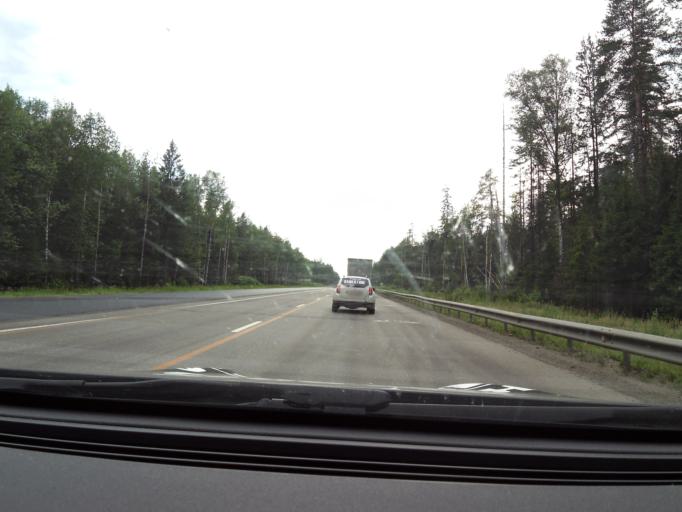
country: RU
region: Vladimir
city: Mstera
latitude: 56.2346
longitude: 41.8535
